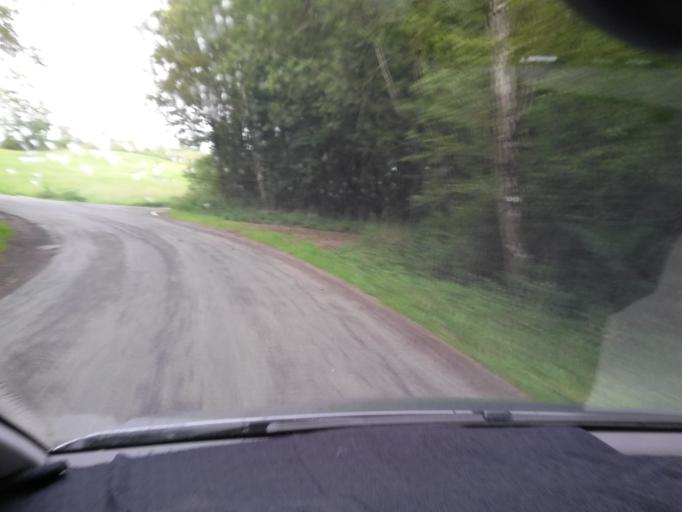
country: BE
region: Wallonia
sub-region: Province du Luxembourg
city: Attert
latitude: 49.7385
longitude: 5.8065
